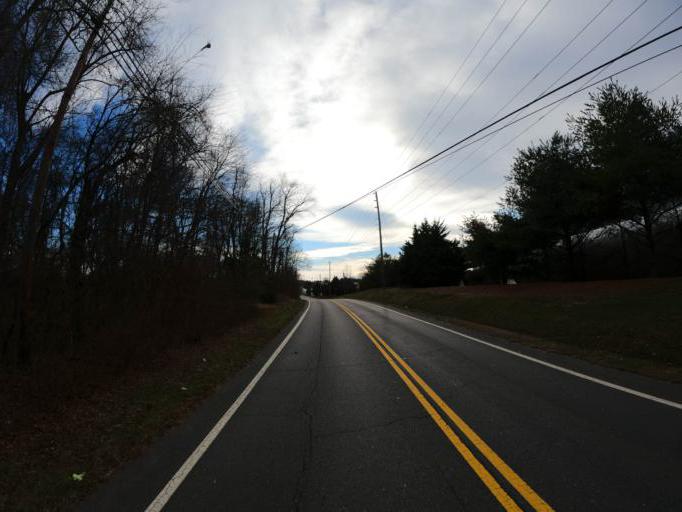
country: US
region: Maryland
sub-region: Montgomery County
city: Clarksburg
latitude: 39.2545
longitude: -77.3013
